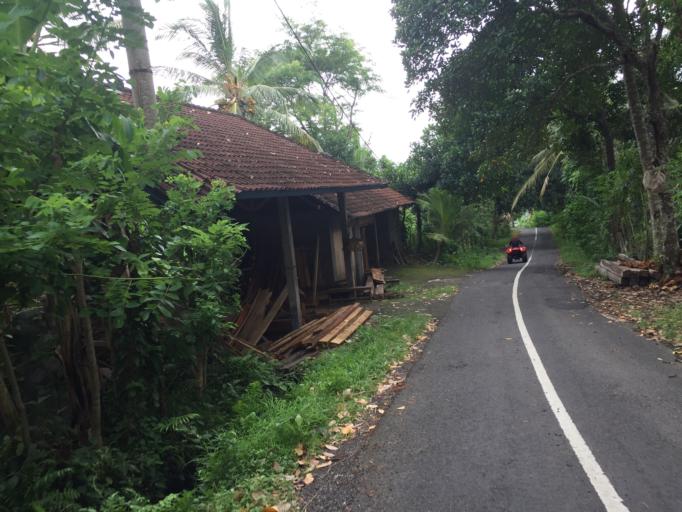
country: ID
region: Bali
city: Banjar Kawan
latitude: -8.4718
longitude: 115.5185
